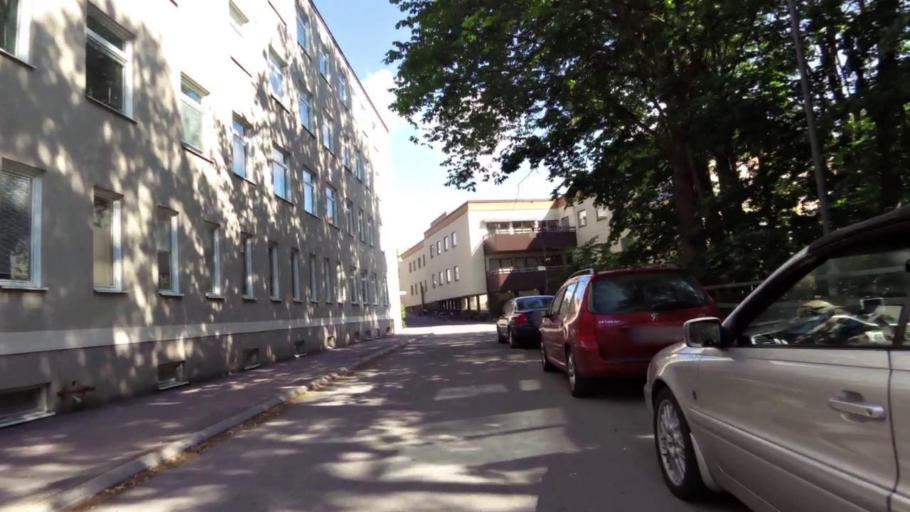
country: SE
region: OEstergoetland
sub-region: Linkopings Kommun
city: Linkoping
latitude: 58.4004
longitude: 15.6242
